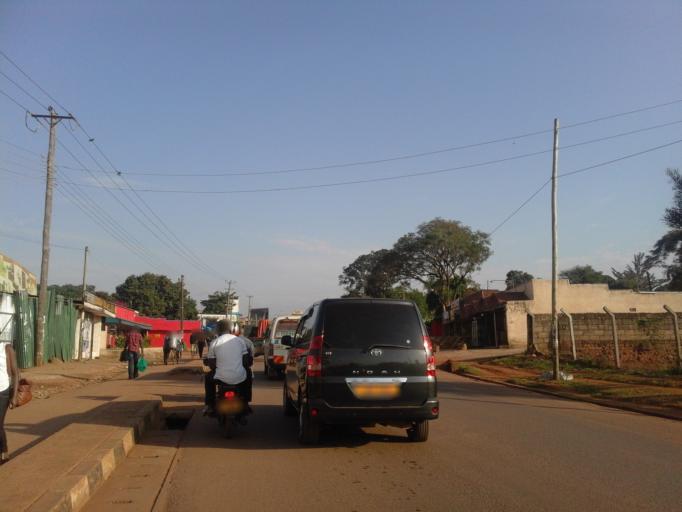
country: UG
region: Central Region
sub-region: Kampala District
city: Kampala
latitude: 0.2849
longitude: 32.6085
